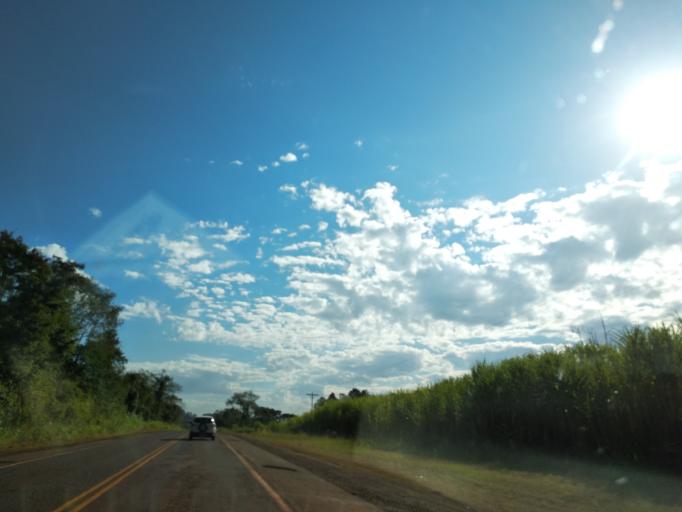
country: AR
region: Misiones
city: Ruiz de Montoya
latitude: -27.0590
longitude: -55.0236
